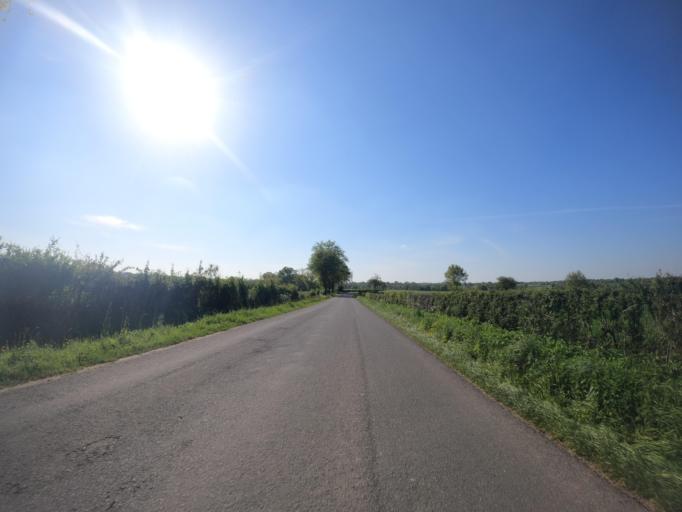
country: FR
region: Poitou-Charentes
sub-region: Departement des Deux-Sevres
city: Moncoutant
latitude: 46.6966
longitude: -0.5451
